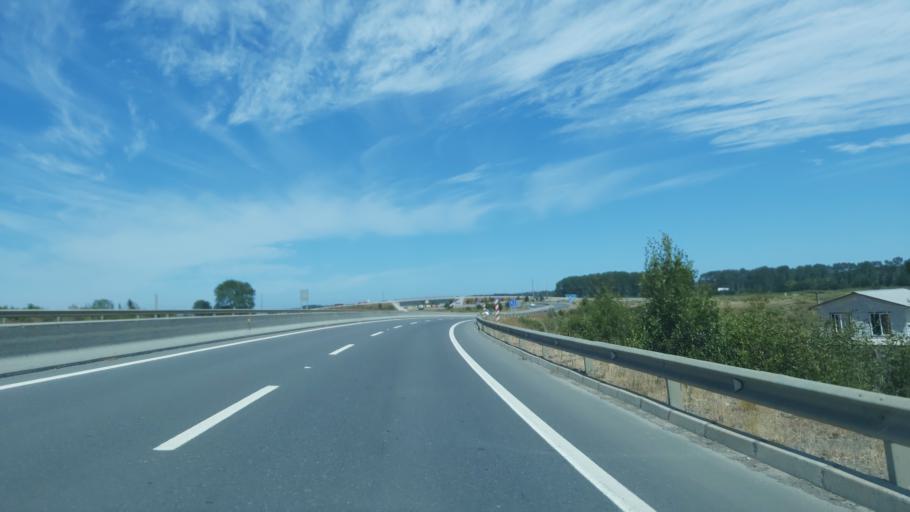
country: CL
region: Biobio
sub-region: Provincia de Concepcion
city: Lota
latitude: -37.1849
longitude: -73.1899
